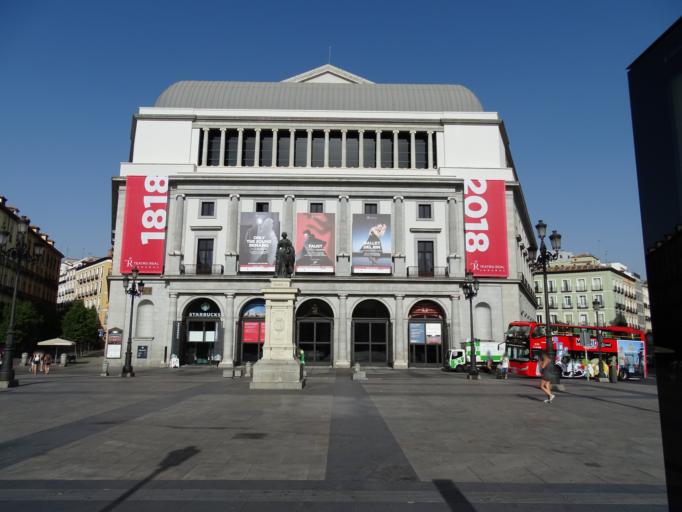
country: ES
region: Madrid
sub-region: Provincia de Madrid
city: City Center
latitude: 40.4181
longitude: -3.7093
